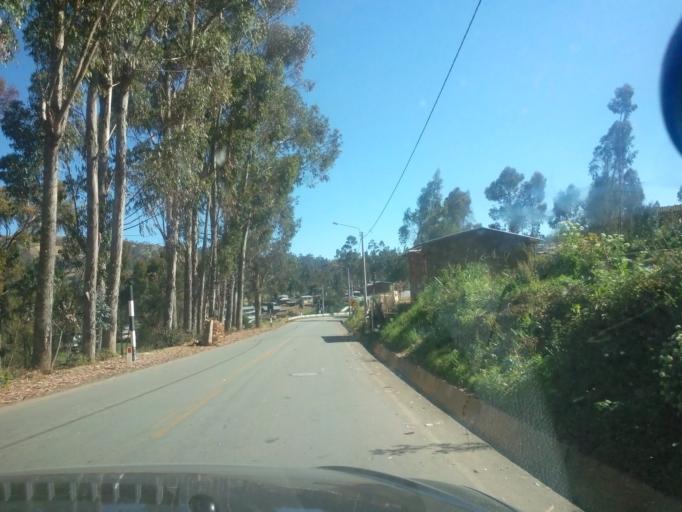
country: PE
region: Apurimac
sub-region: Provincia de Andahuaylas
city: Talavera
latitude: -13.6502
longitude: -73.5139
